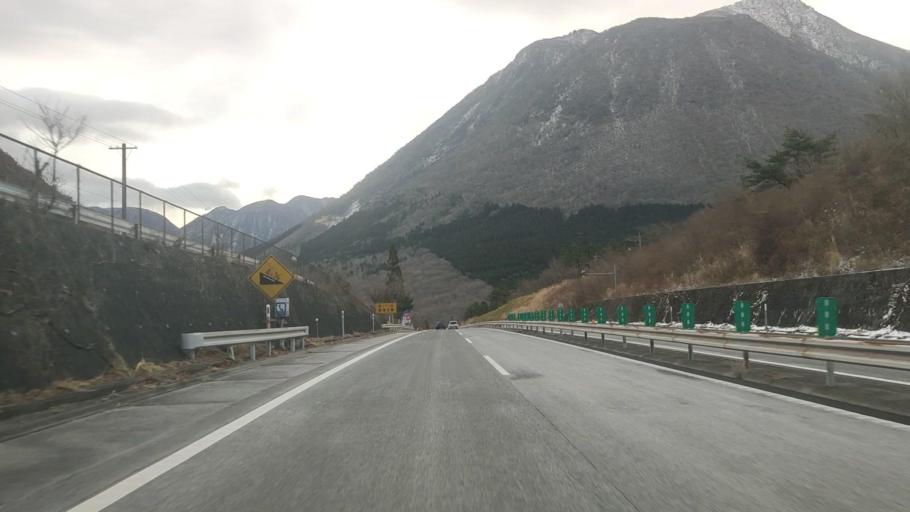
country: JP
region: Oita
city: Beppu
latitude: 33.2958
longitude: 131.3672
